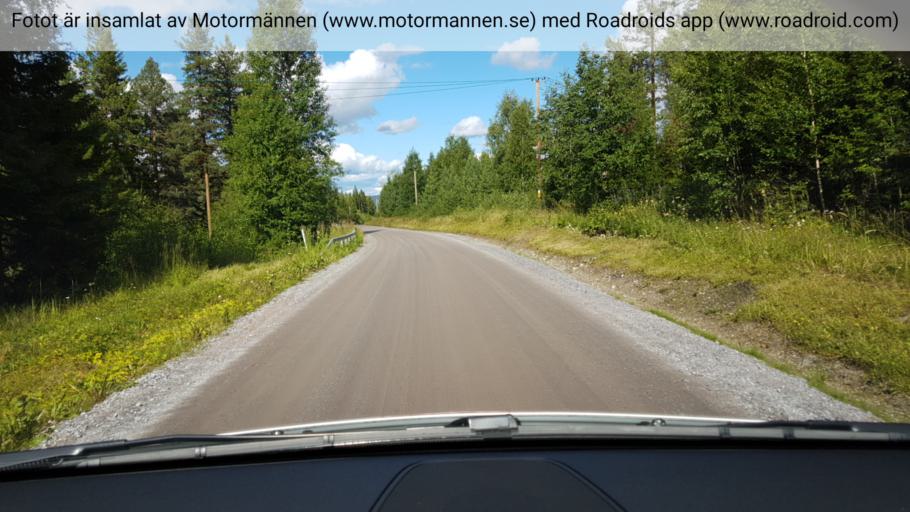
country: SE
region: Jaemtland
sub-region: Braecke Kommun
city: Braecke
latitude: 63.1345
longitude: 15.7583
